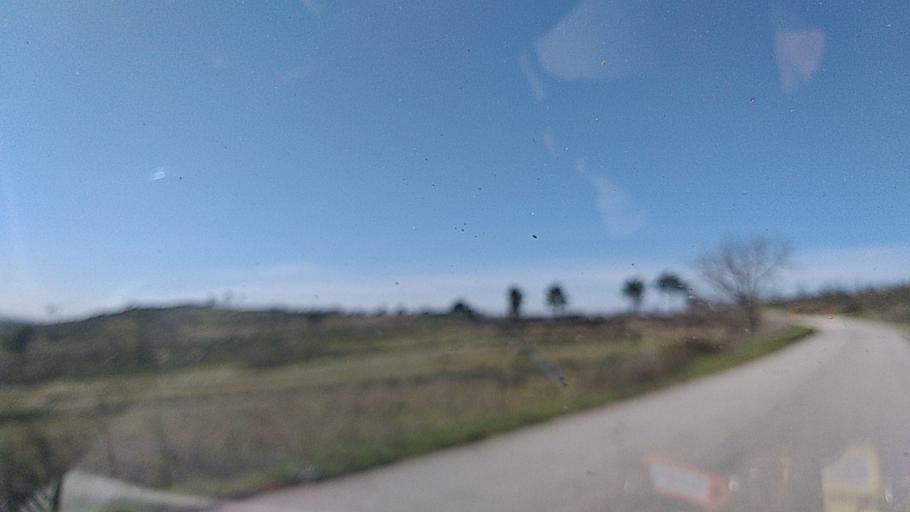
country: PT
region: Guarda
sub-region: Celorico da Beira
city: Celorico da Beira
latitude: 40.5918
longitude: -7.4562
